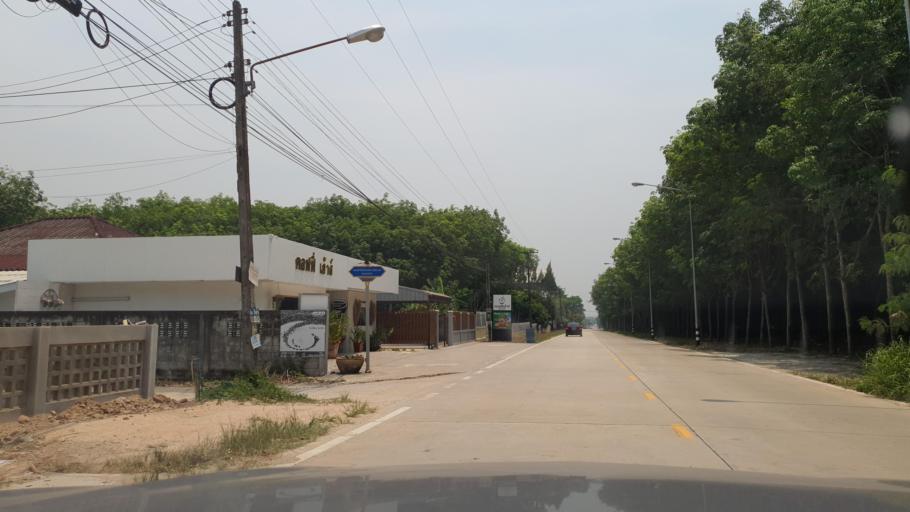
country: TH
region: Rayong
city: Nikhom Phattana
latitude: 12.7900
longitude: 101.1592
